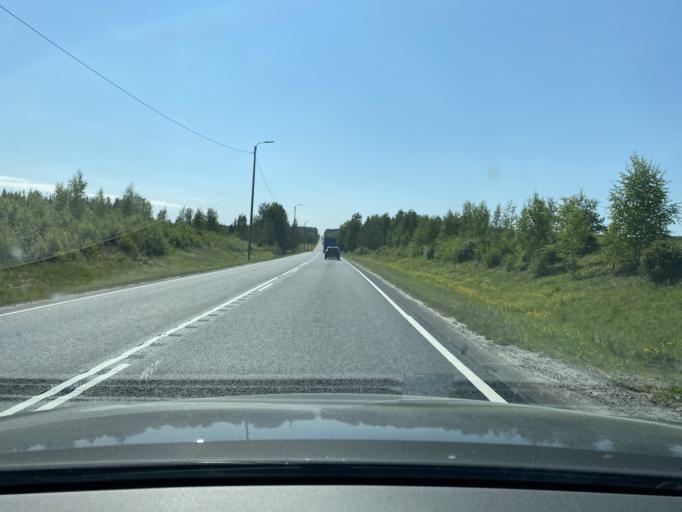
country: FI
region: Pirkanmaa
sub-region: Lounais-Pirkanmaa
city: Mouhijaervi
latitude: 61.3643
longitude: 23.1048
